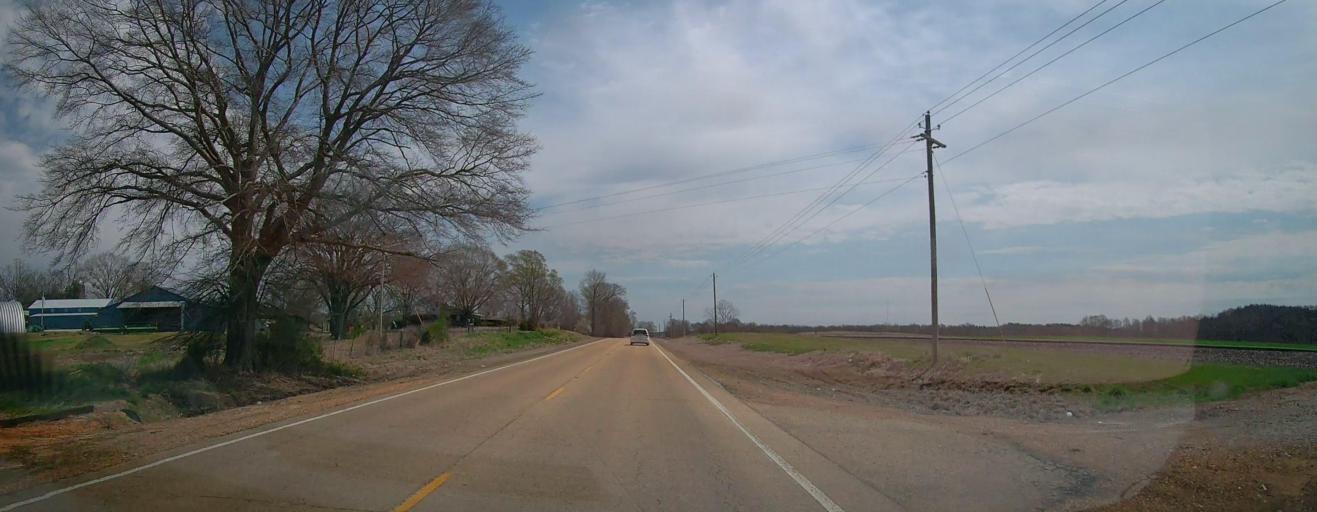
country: US
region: Mississippi
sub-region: Benton County
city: Ashland
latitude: 34.6212
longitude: -89.2327
